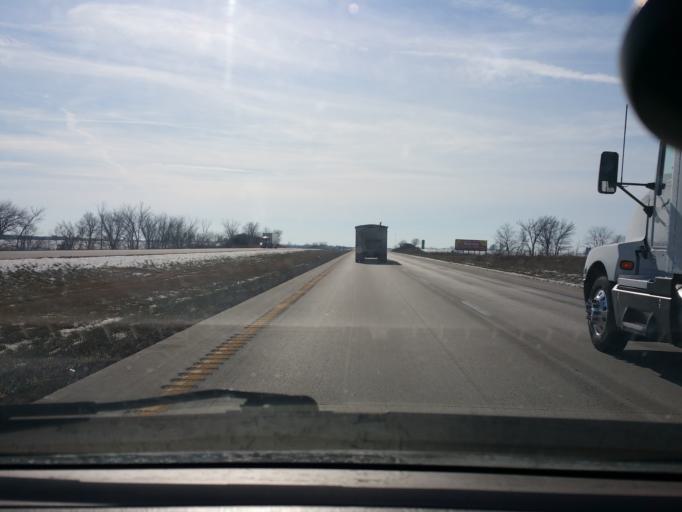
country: US
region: Missouri
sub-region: Clinton County
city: Cameron
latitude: 39.6460
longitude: -94.2413
